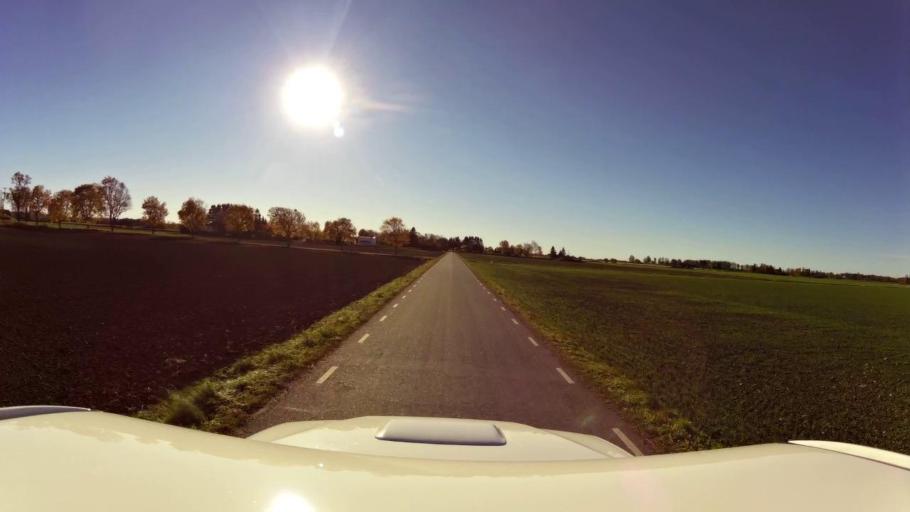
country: SE
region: OEstergoetland
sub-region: Linkopings Kommun
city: Ljungsbro
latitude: 58.4966
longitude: 15.4185
